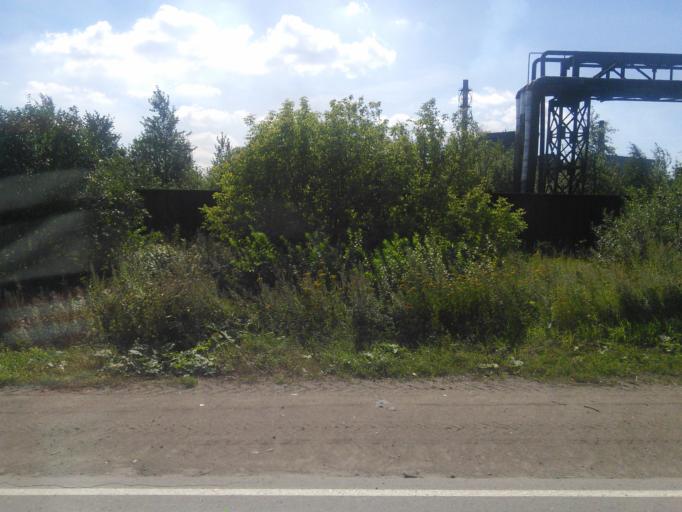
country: RU
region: Vologda
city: Cherepovets
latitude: 59.1536
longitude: 37.8737
